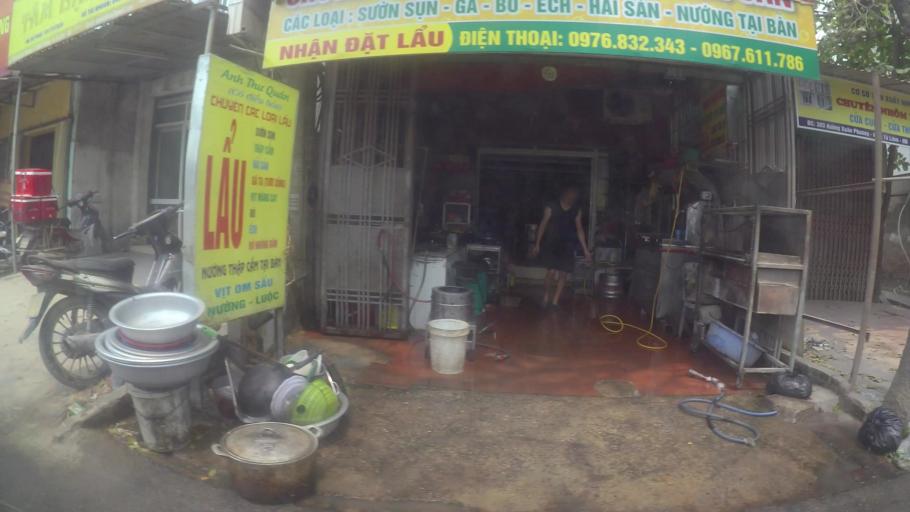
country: VN
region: Ha Noi
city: Cau Dien
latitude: 21.0327
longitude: 105.7390
